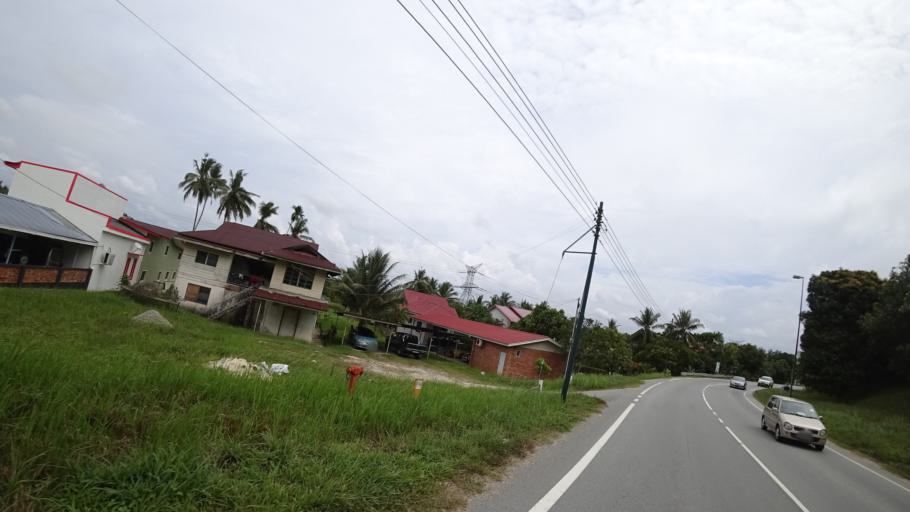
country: BN
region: Tutong
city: Tutong
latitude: 4.8072
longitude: 114.6724
